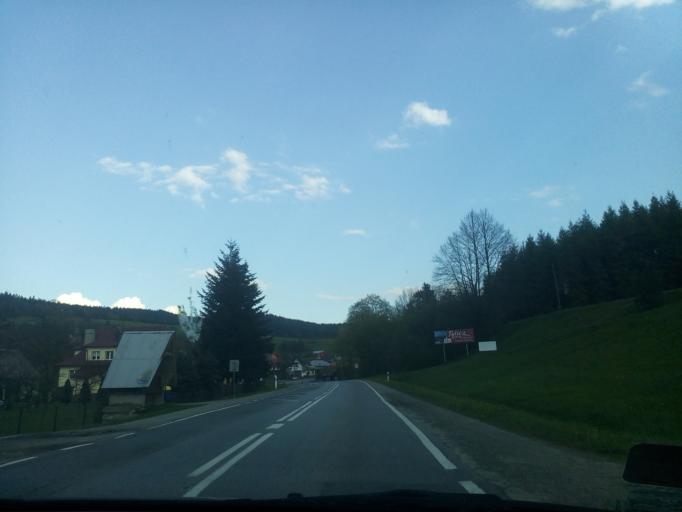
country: PL
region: Lesser Poland Voivodeship
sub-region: Powiat nowosadecki
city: Labowa
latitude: 49.4974
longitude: 20.9035
